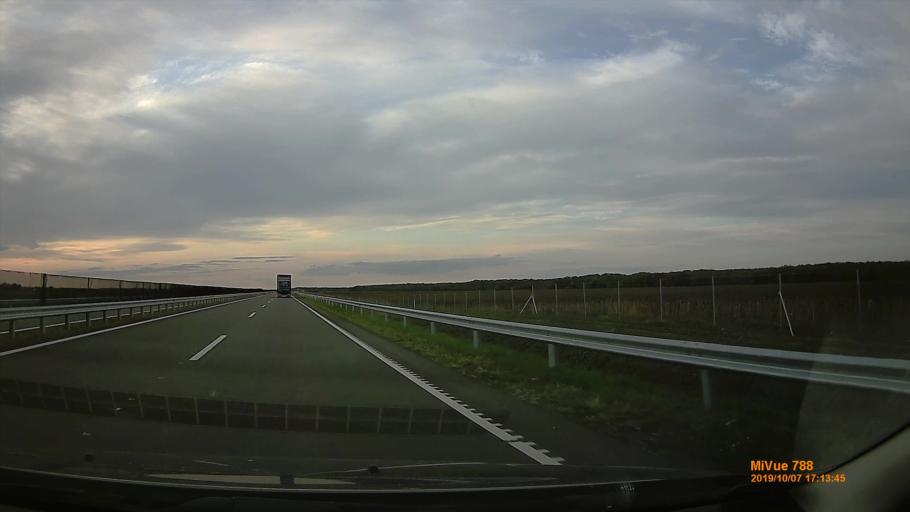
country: HU
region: Jasz-Nagykun-Szolnok
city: Kunszentmarton
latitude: 46.8239
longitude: 20.3652
